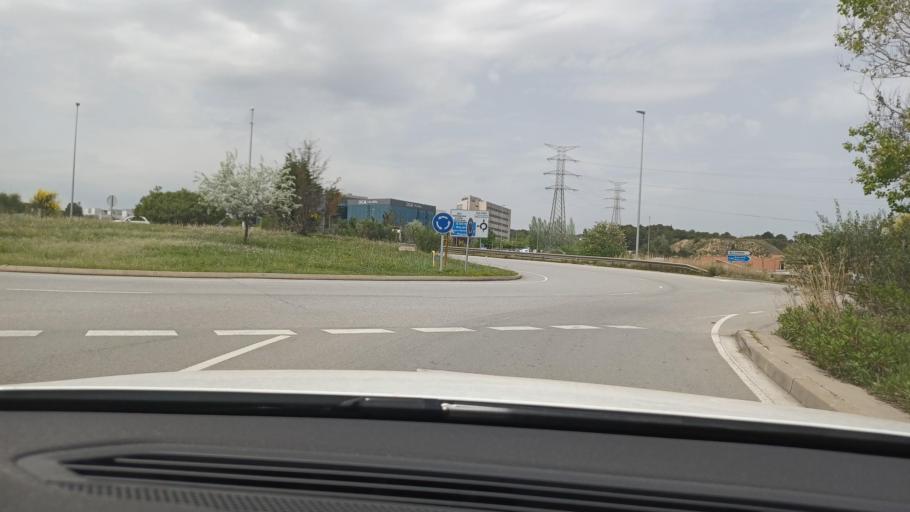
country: ES
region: Catalonia
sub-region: Provincia de Barcelona
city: Sant Cugat del Valles
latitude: 41.4873
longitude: 2.0838
